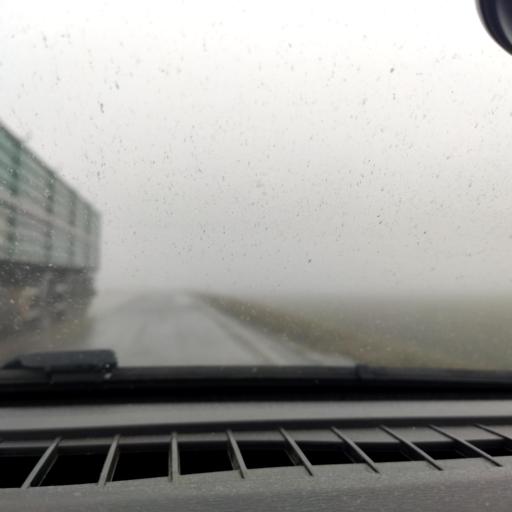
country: RU
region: Belgorod
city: Ilovka
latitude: 50.7210
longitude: 38.6782
